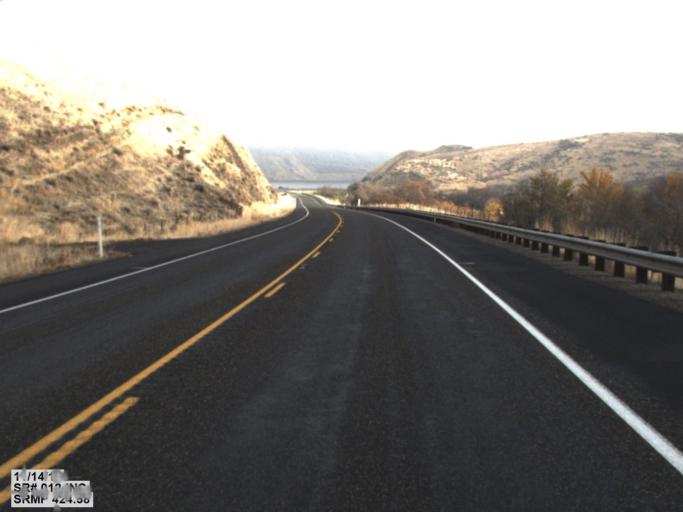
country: US
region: Washington
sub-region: Asotin County
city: Clarkston Heights-Vineland
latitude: 46.4080
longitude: -117.2203
